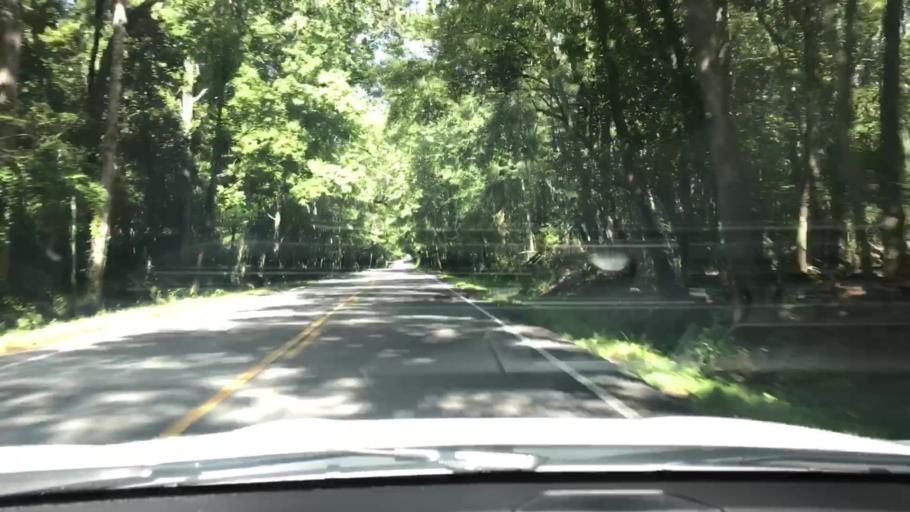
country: US
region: South Carolina
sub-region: Berkeley County
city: Hanahan
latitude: 32.8824
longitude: -80.1047
